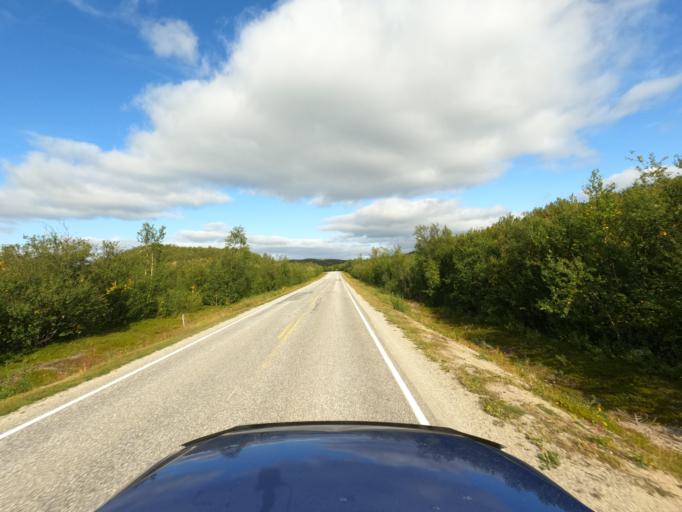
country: NO
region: Finnmark Fylke
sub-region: Porsanger
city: Lakselv
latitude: 69.9650
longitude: 24.9678
